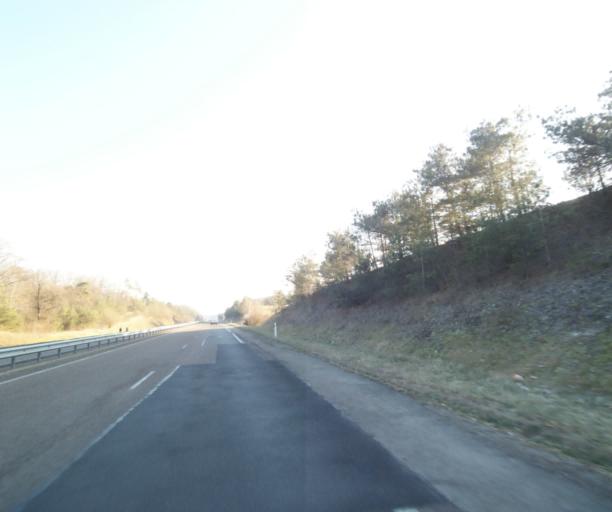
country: FR
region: Champagne-Ardenne
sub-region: Departement de la Haute-Marne
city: Chevillon
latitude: 48.5083
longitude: 5.0969
